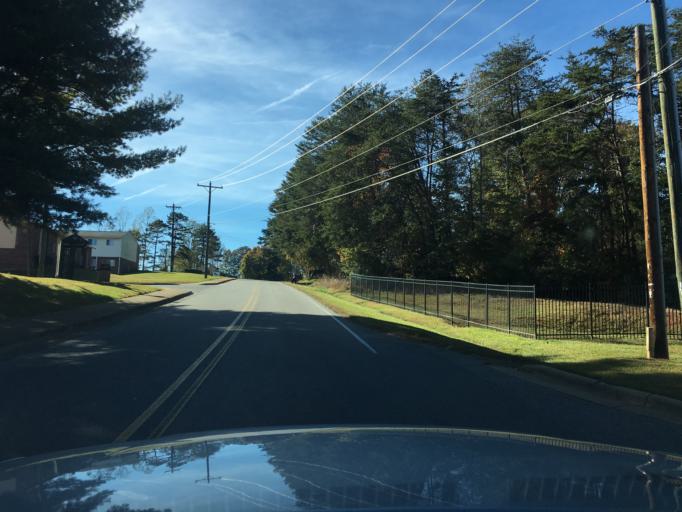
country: US
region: North Carolina
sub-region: Catawba County
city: Saint Stephens
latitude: 35.7094
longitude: -81.2745
